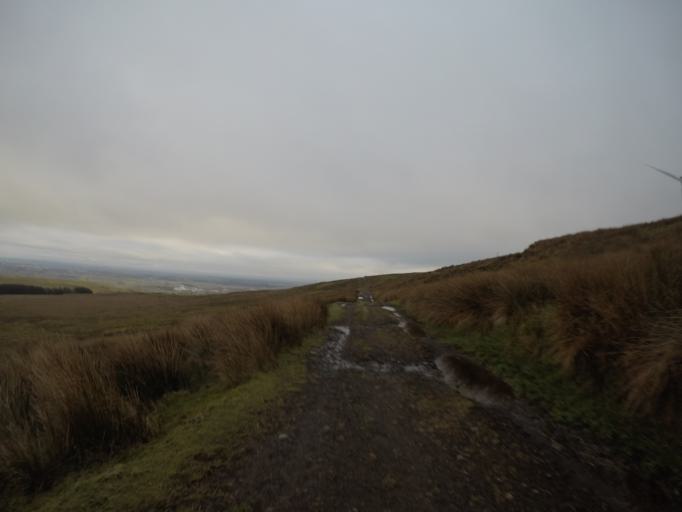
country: GB
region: Scotland
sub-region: North Ayrshire
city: Dalry
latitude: 55.7361
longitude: -4.7695
